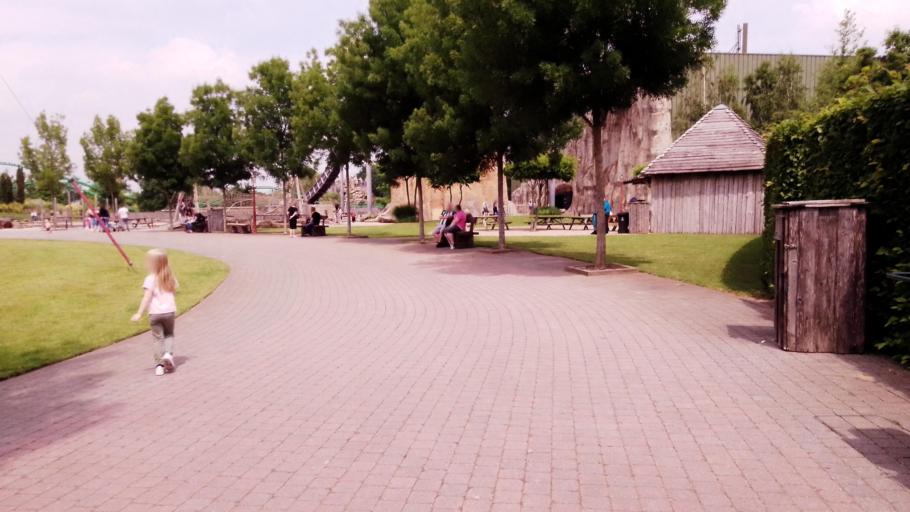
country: NL
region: Limburg
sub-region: Gemeente Peel en Maas
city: Maasbree
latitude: 51.3963
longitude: 5.9854
